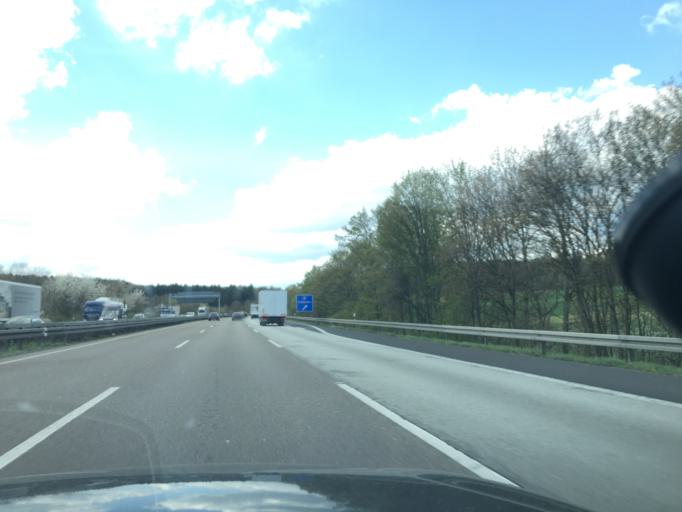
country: DE
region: Hesse
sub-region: Regierungsbezirk Giessen
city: Langgons
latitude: 50.4810
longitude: 8.7024
